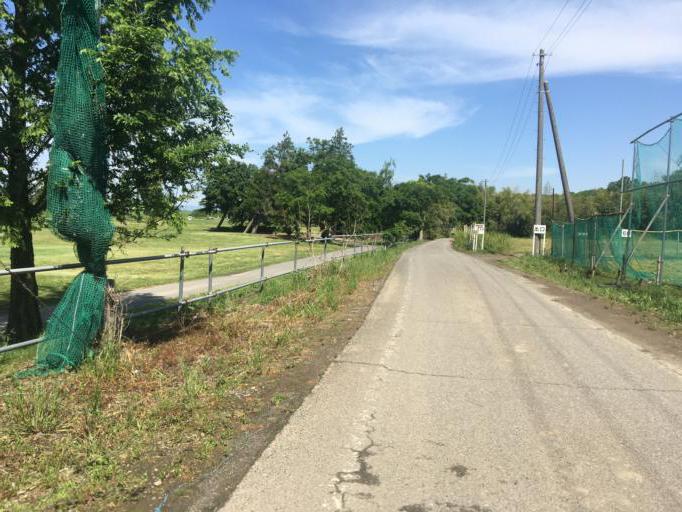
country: JP
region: Saitama
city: Shiki
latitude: 35.8604
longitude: 139.5885
